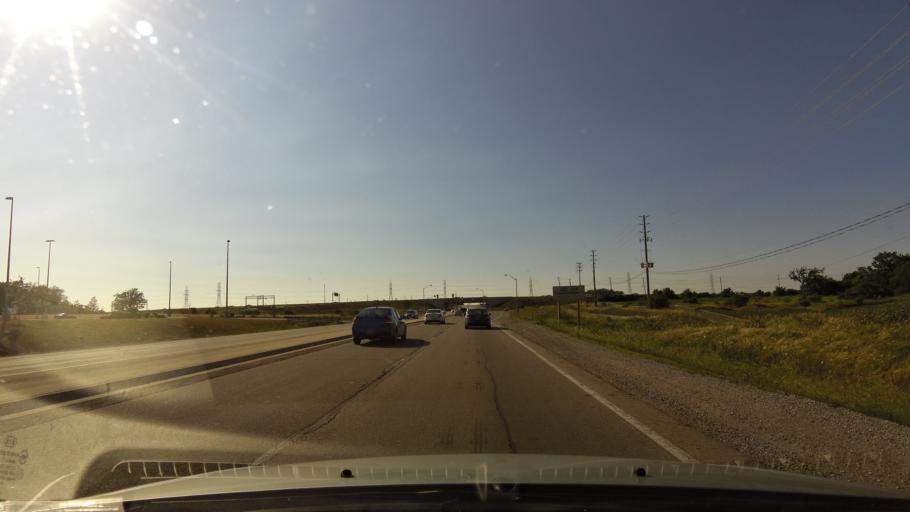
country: CA
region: Ontario
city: Oakville
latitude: 43.5064
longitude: -79.7445
